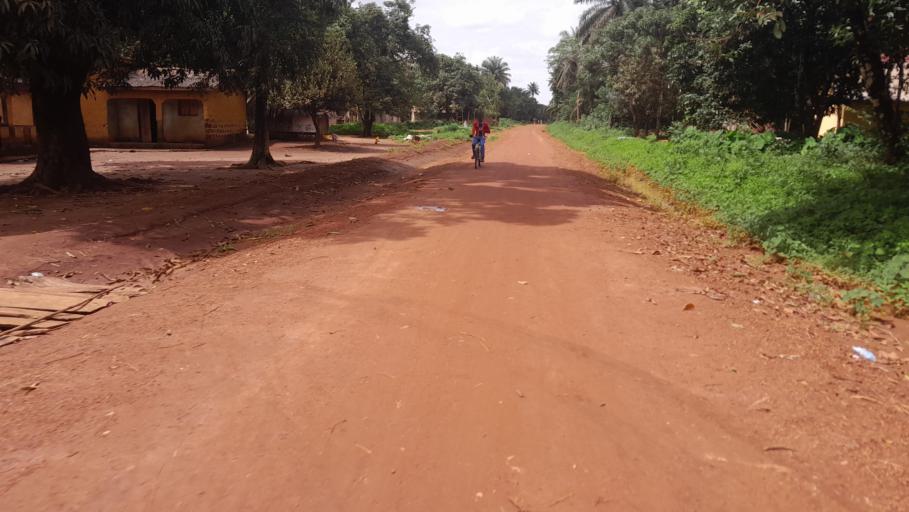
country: GN
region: Boke
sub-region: Boffa
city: Boffa
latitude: 10.0152
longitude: -13.8883
